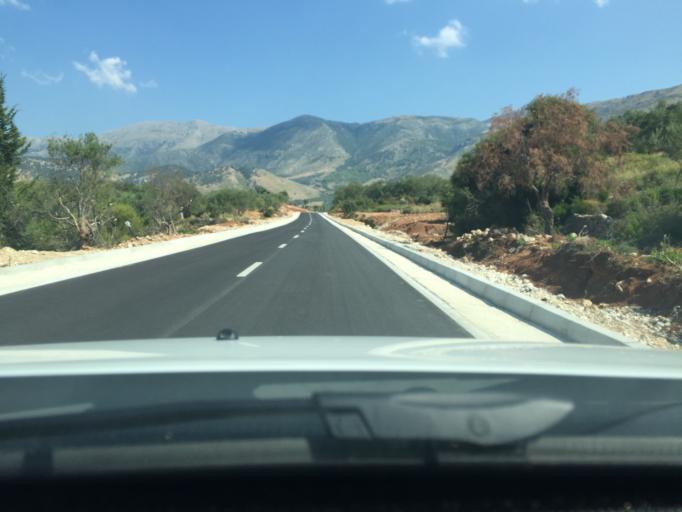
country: AL
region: Vlore
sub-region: Rrethi i Vlores
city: Himare
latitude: 40.0991
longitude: 19.7607
